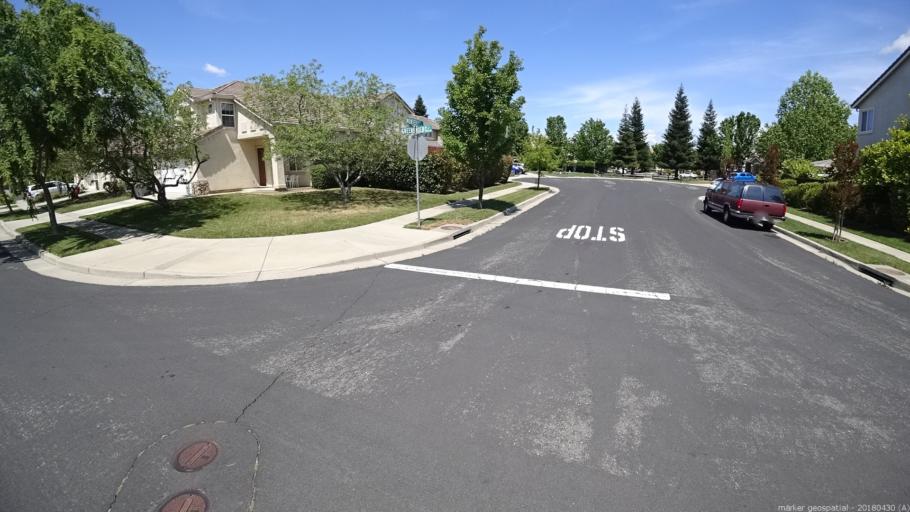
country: US
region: California
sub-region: Yolo County
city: West Sacramento
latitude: 38.5487
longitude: -121.5247
